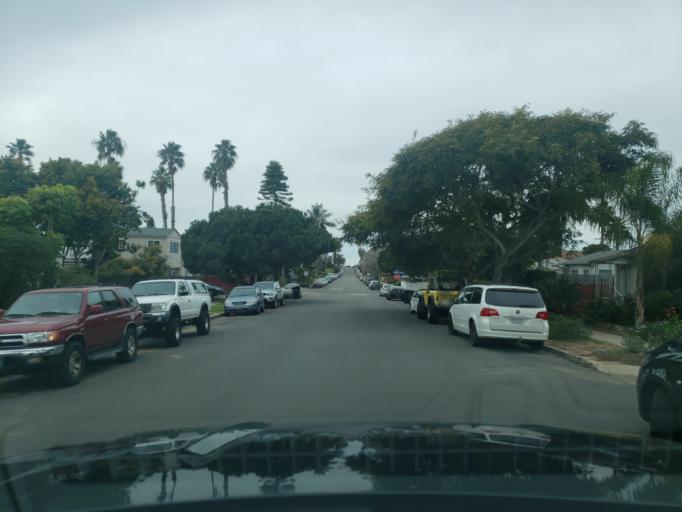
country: US
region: California
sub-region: San Diego County
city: Coronado
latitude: 32.7393
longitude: -117.2513
